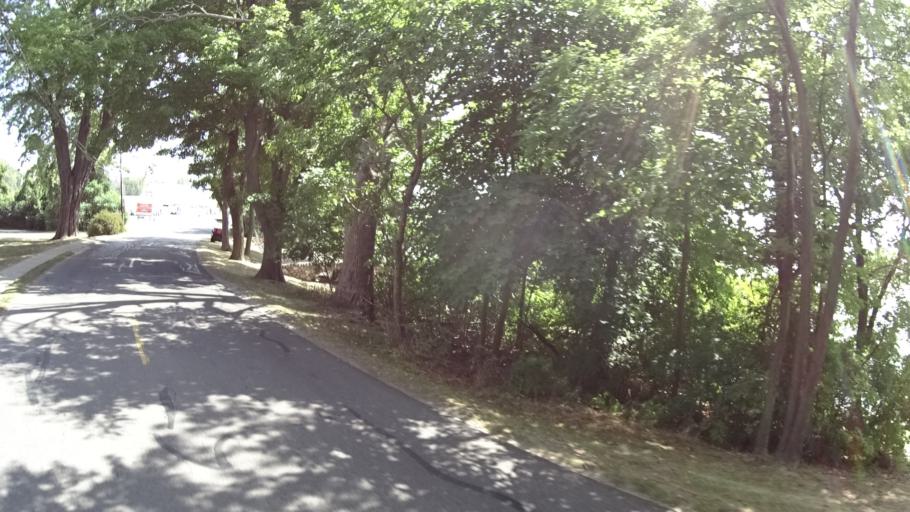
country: US
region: Ohio
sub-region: Erie County
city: Sandusky
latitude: 41.5924
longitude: -82.7053
